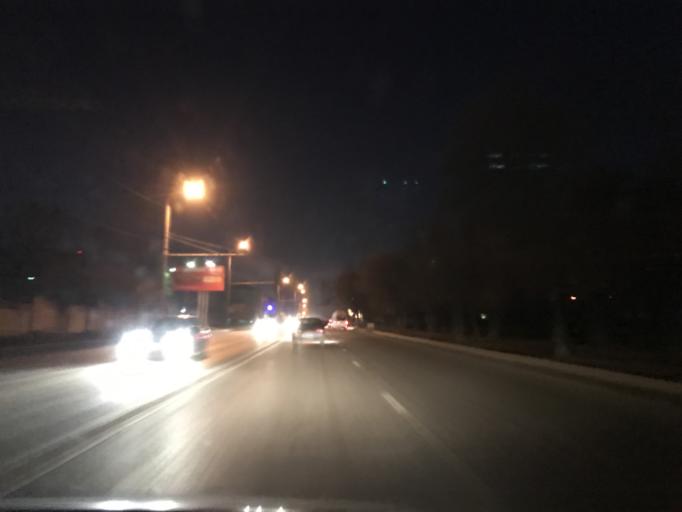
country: RU
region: Rostov
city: Kalinin
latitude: 47.2050
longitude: 39.6136
